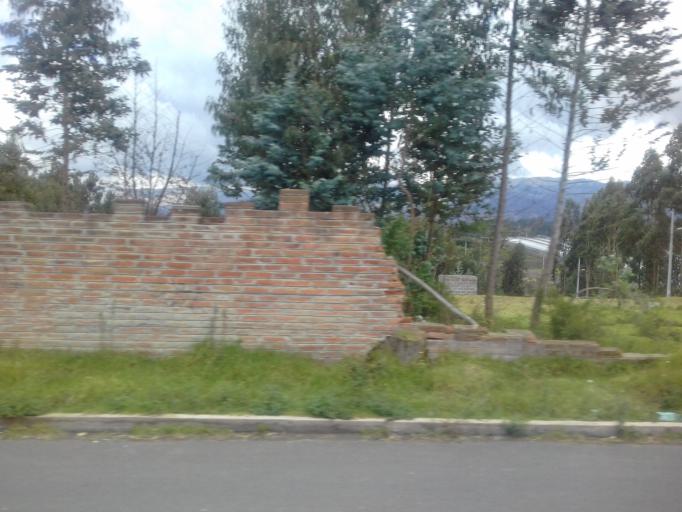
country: EC
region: Pichincha
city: Sangolqui
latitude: -0.3373
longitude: -78.4134
